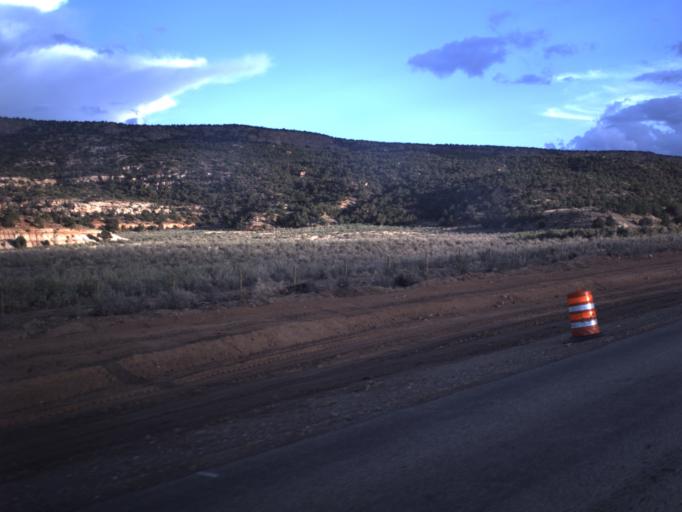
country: US
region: Utah
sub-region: San Juan County
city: Monticello
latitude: 38.0330
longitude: -109.3455
